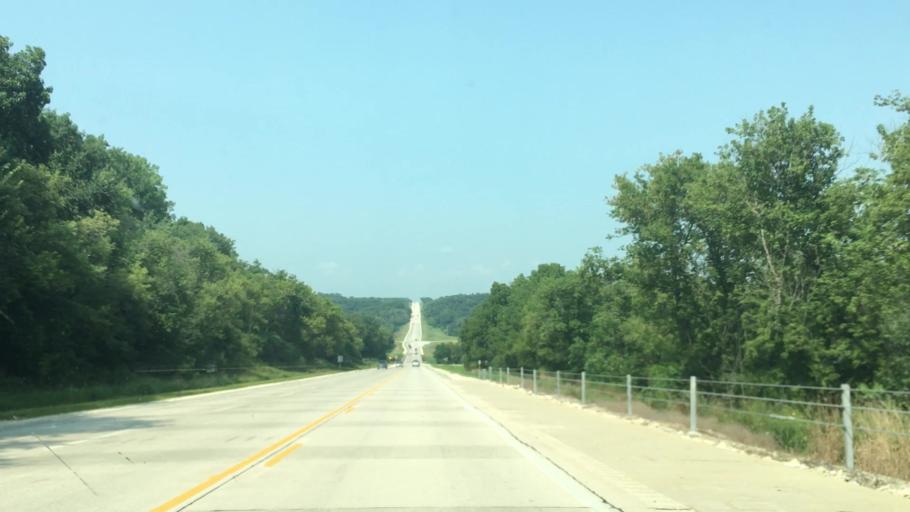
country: US
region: Iowa
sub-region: Winneshiek County
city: Decorah
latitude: 43.3113
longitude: -91.8148
